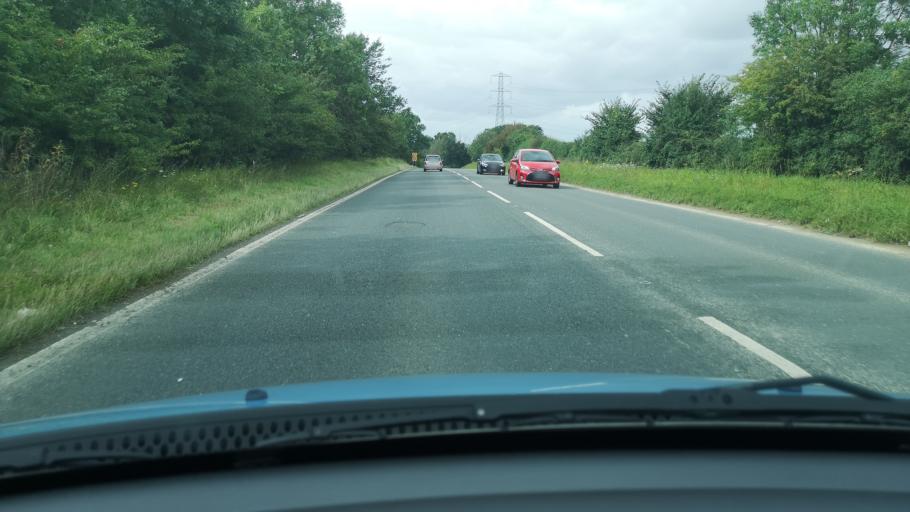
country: GB
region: England
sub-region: Doncaster
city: Marr
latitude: 53.5838
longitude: -1.2326
